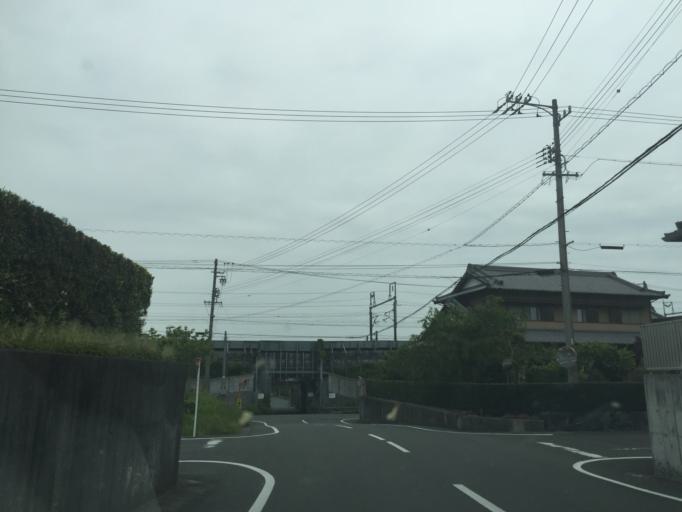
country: JP
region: Shizuoka
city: Kakegawa
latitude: 34.7638
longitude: 137.9942
